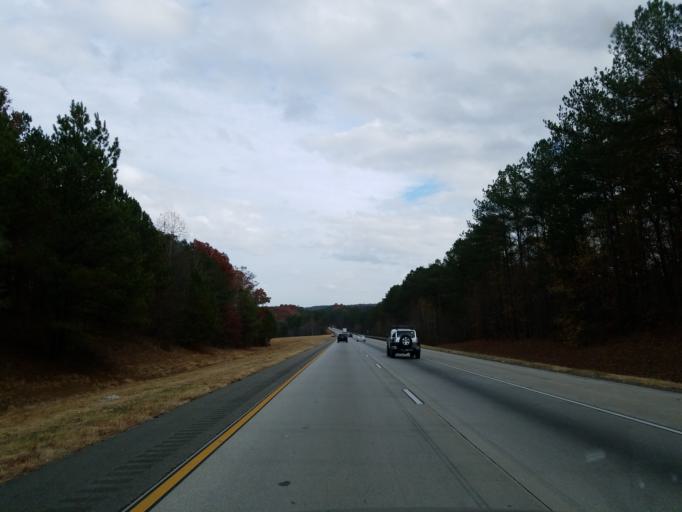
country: US
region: Georgia
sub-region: Carroll County
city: Mount Zion
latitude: 33.6872
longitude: -85.2344
